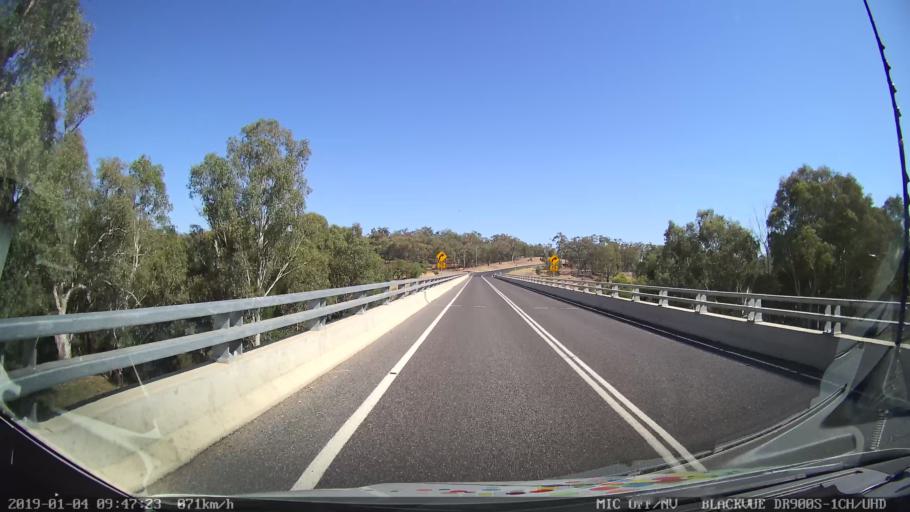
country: AU
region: New South Wales
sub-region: Cabonne
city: Canowindra
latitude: -33.6069
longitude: 148.4322
